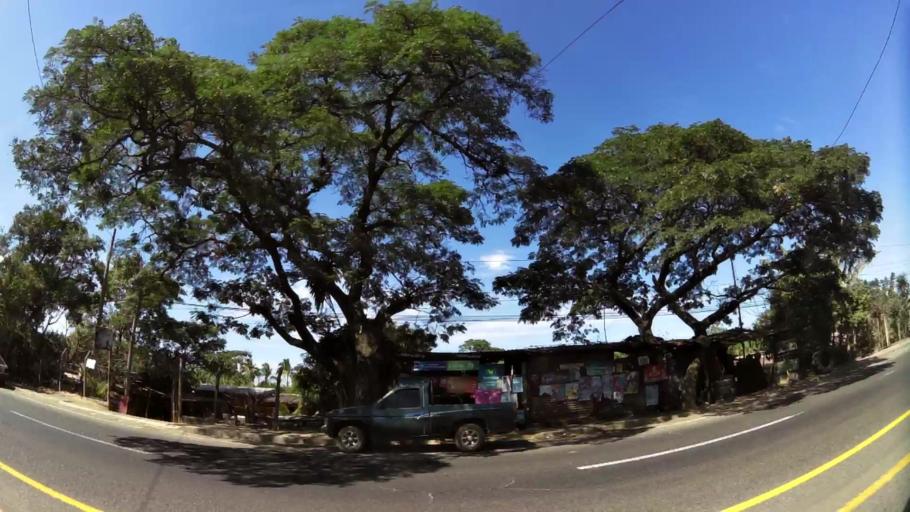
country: SV
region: Ahuachapan
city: Atiquizaya
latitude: 13.9692
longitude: -89.7539
